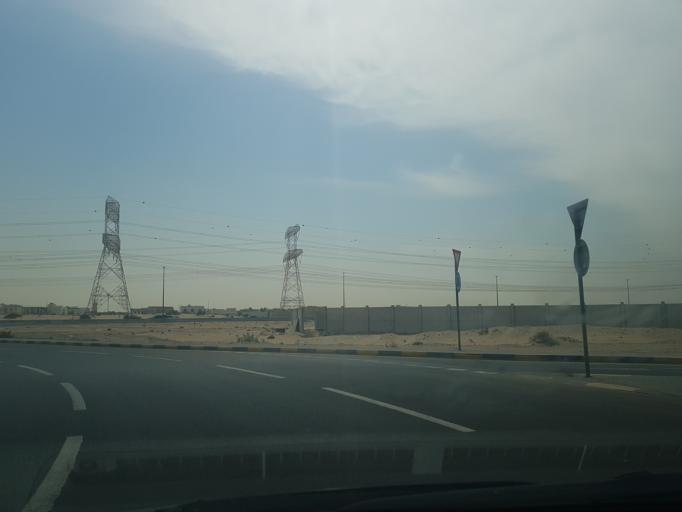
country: AE
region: Ash Shariqah
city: Sharjah
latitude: 25.2674
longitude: 55.4835
